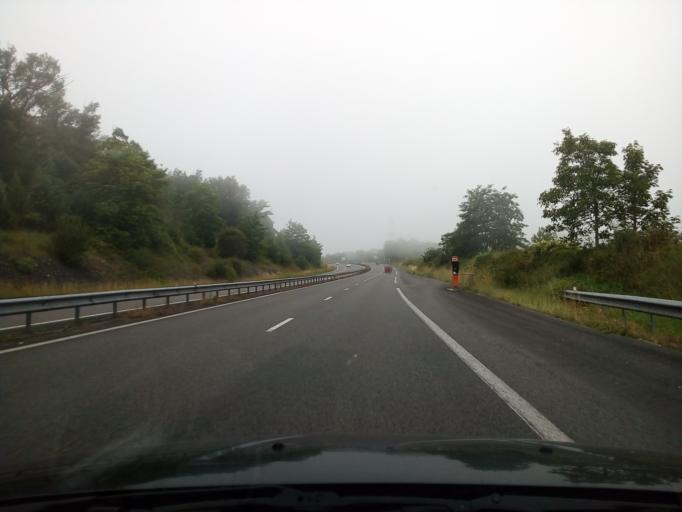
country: FR
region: Poitou-Charentes
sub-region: Departement de la Charente
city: Jarnac
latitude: 45.6674
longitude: -0.1816
